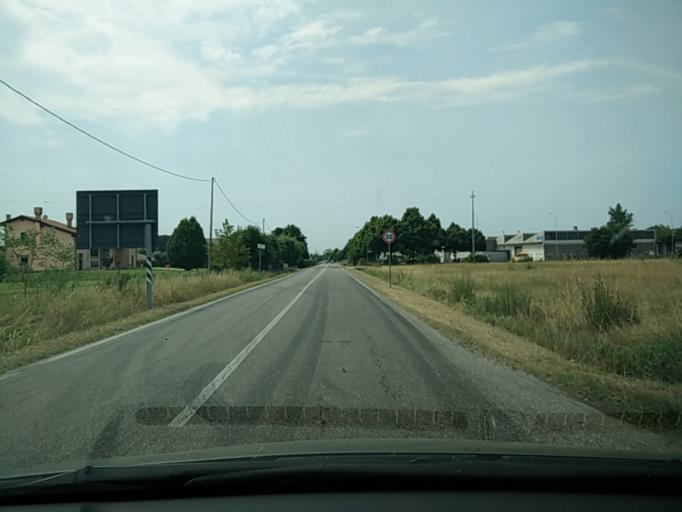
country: IT
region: Veneto
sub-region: Provincia di Treviso
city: Maserada sul Piave
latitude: 45.7678
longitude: 12.2888
